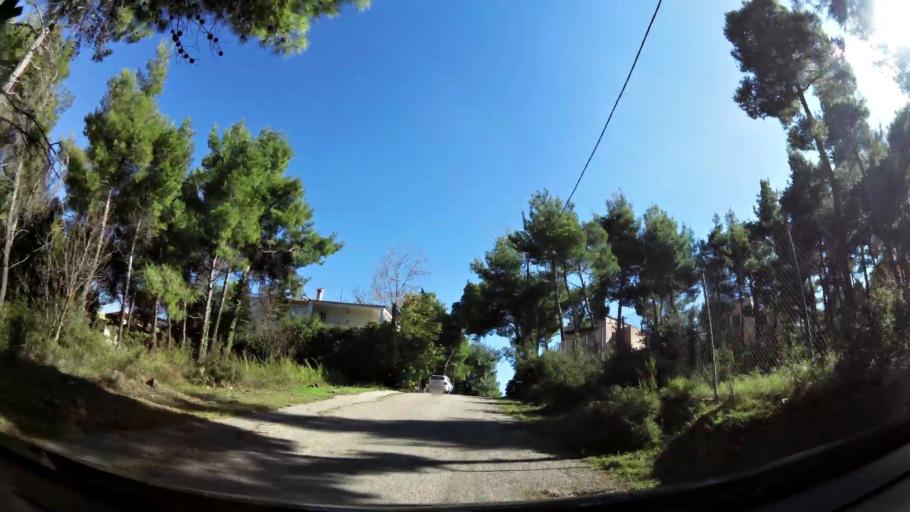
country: GR
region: Attica
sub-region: Nomarchia Anatolikis Attikis
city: Dionysos
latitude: 38.1058
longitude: 23.8801
